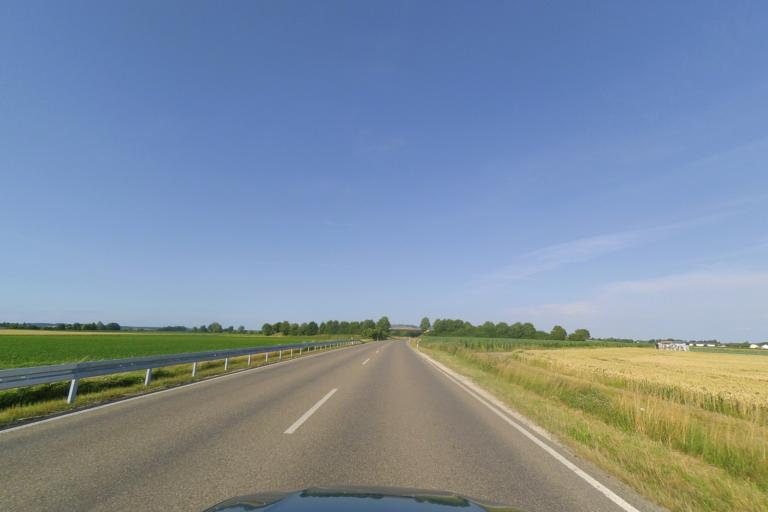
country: DE
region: Bavaria
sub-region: Swabia
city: Gundelfingen
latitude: 48.5617
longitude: 10.3615
